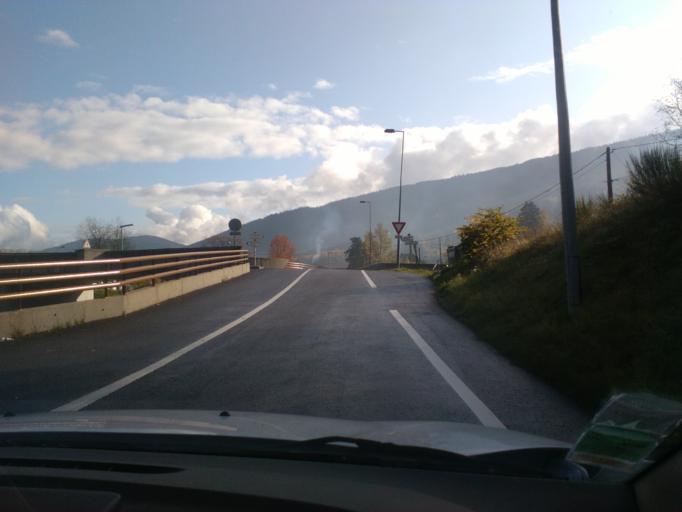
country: FR
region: Lorraine
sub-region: Departement des Vosges
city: Saulxures-sur-Moselotte
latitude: 47.9450
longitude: 6.7679
